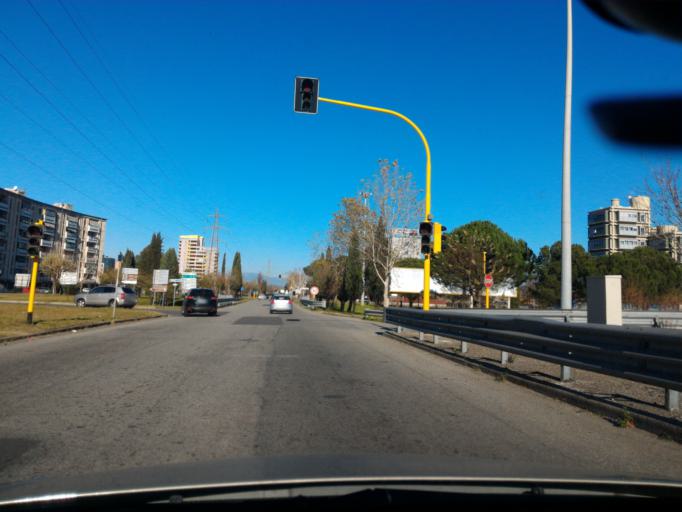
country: IT
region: Calabria
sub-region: Provincia di Cosenza
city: Cosenza
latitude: 39.3176
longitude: 16.2579
